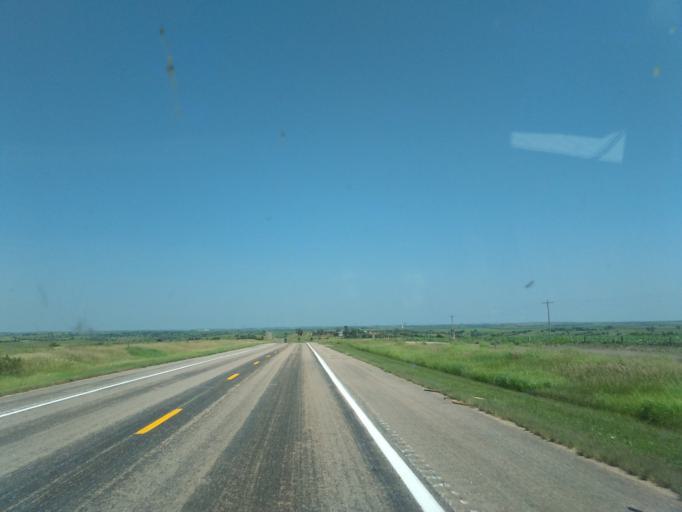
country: US
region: Nebraska
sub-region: Frontier County
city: Stockville
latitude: 40.6105
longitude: -100.6298
